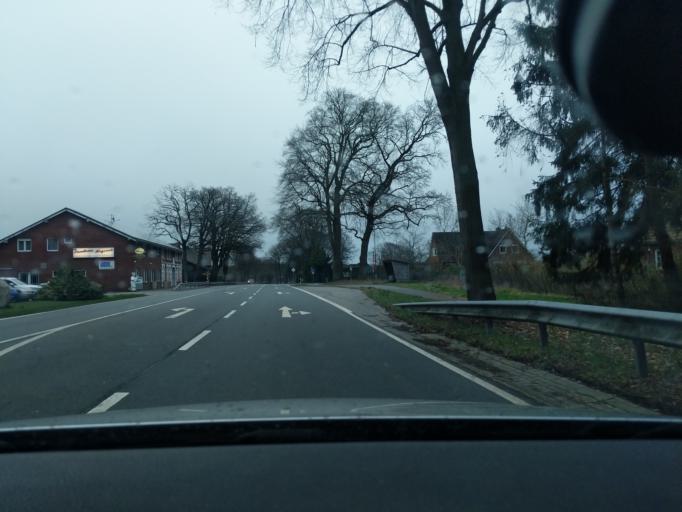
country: DE
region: Lower Saxony
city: Heinbockel
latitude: 53.5429
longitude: 9.3204
